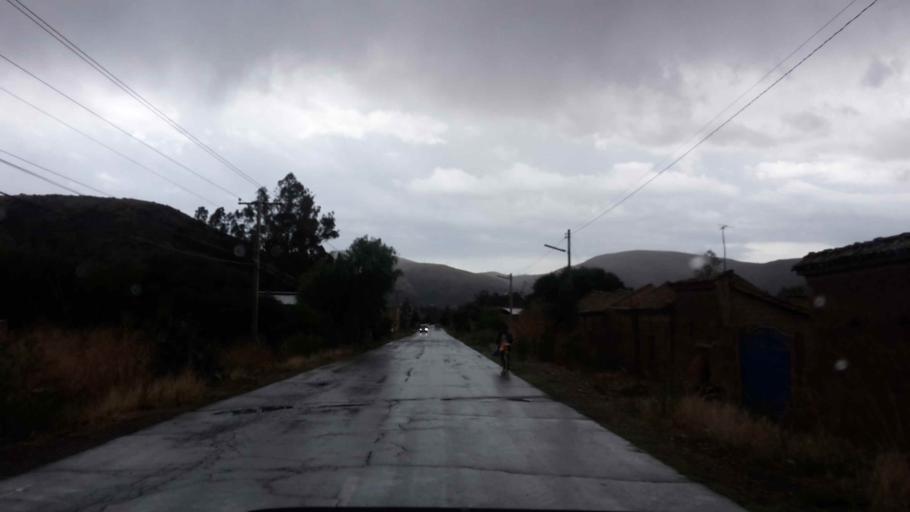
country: BO
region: Cochabamba
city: Tarata
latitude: -17.5494
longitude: -66.0974
